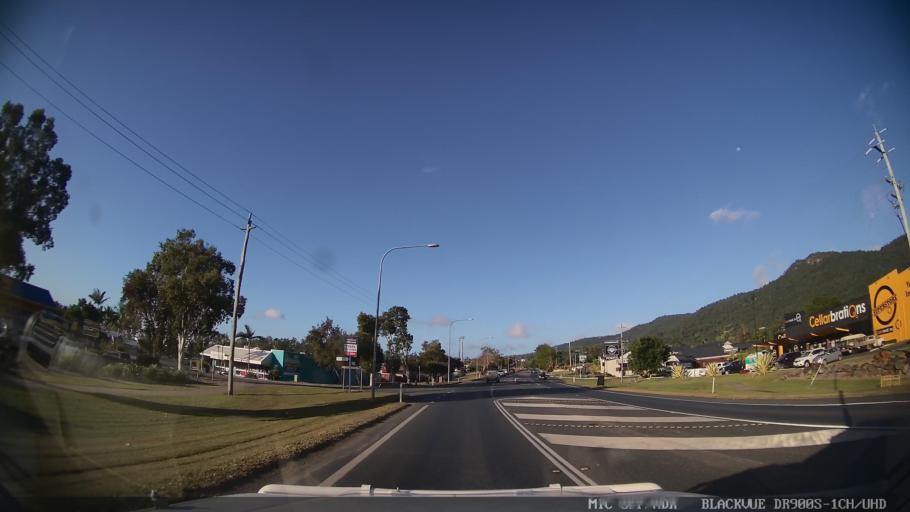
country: AU
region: Queensland
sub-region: Whitsunday
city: Proserpine
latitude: -20.2864
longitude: 148.6803
